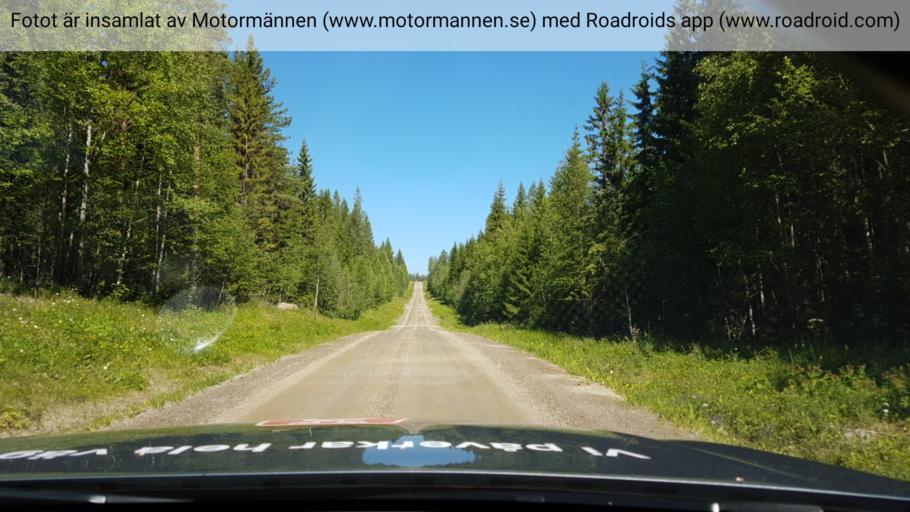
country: SE
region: Jaemtland
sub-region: Braecke Kommun
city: Braecke
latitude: 62.8151
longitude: 15.2235
